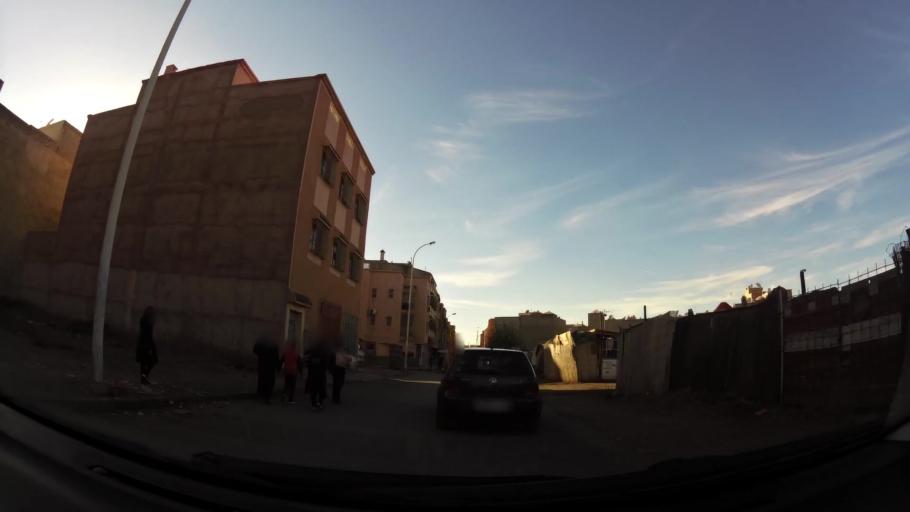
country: MA
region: Marrakech-Tensift-Al Haouz
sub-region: Marrakech
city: Marrakesh
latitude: 31.6171
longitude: -8.0590
